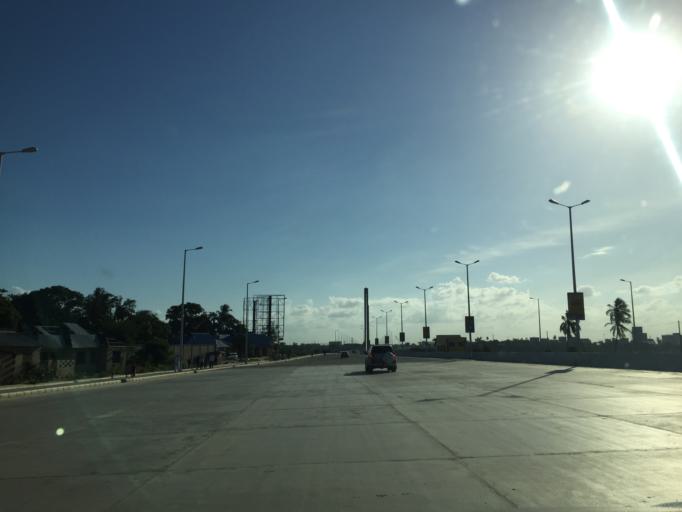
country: TZ
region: Dar es Salaam
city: Dar es Salaam
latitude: -6.8596
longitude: 39.3055
